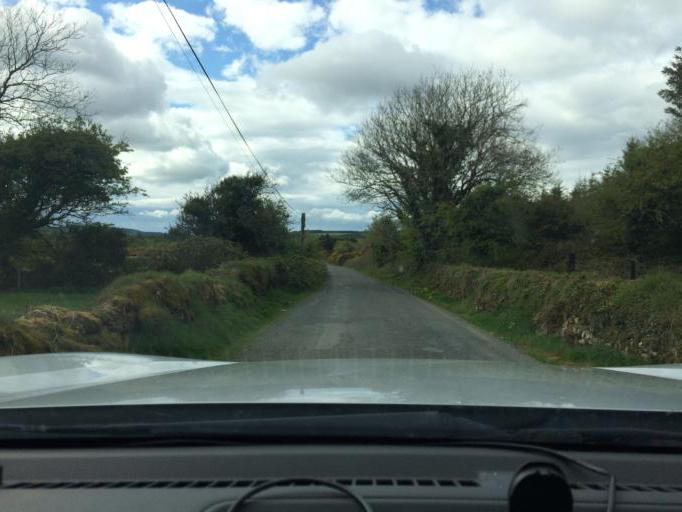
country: IE
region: Munster
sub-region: Waterford
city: Dungarvan
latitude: 52.0434
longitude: -7.6520
